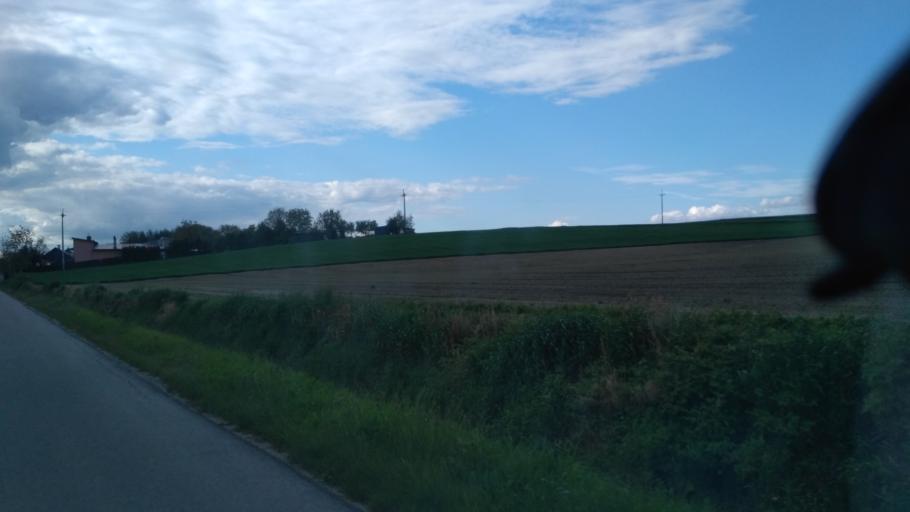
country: PL
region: Subcarpathian Voivodeship
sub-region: Powiat jaroslawski
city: Pawlosiow
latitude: 49.9554
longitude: 22.6551
